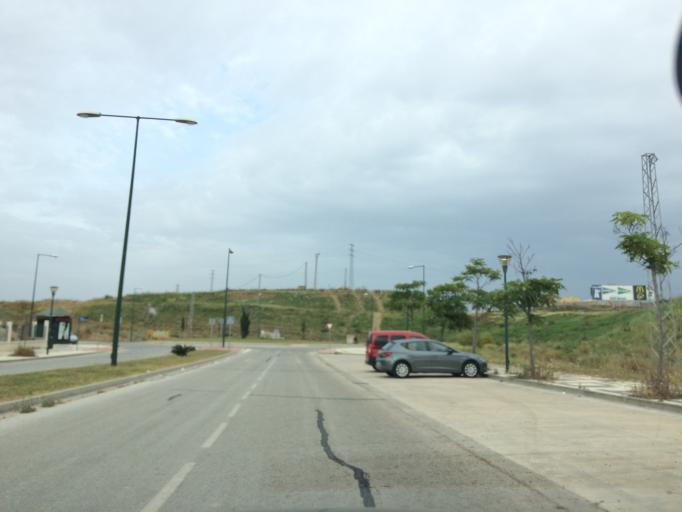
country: ES
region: Andalusia
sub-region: Provincia de Malaga
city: Malaga
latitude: 36.7147
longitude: -4.4908
